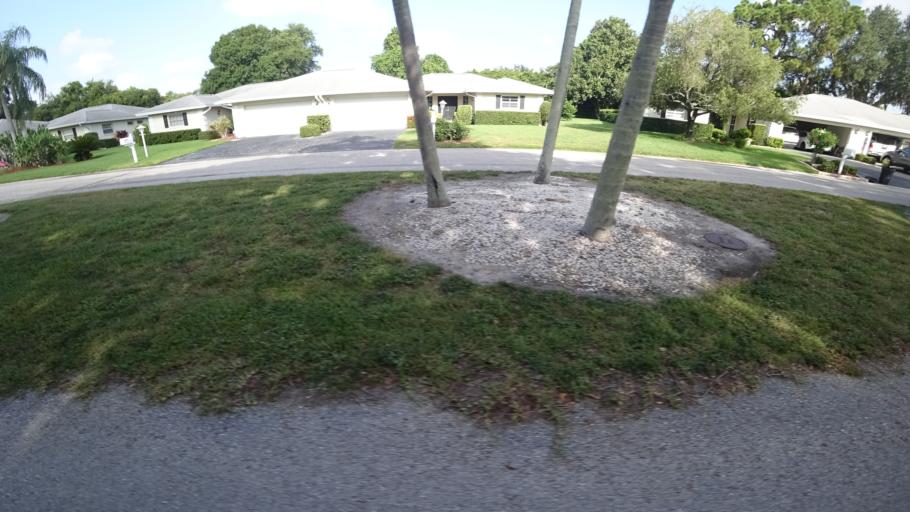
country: US
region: Florida
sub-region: Sarasota County
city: Desoto Lakes
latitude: 27.4130
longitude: -82.4971
